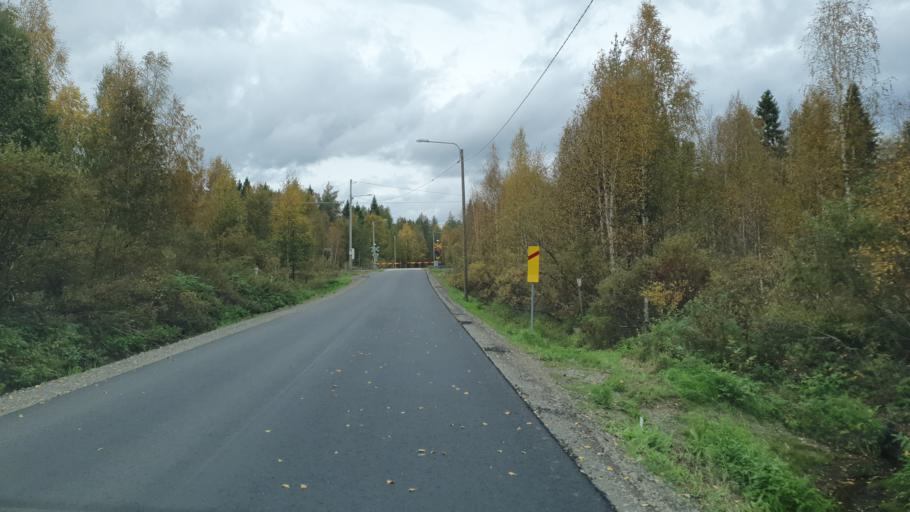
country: FI
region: Lapland
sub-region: Rovaniemi
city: Rovaniemi
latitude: 66.4201
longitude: 25.4097
